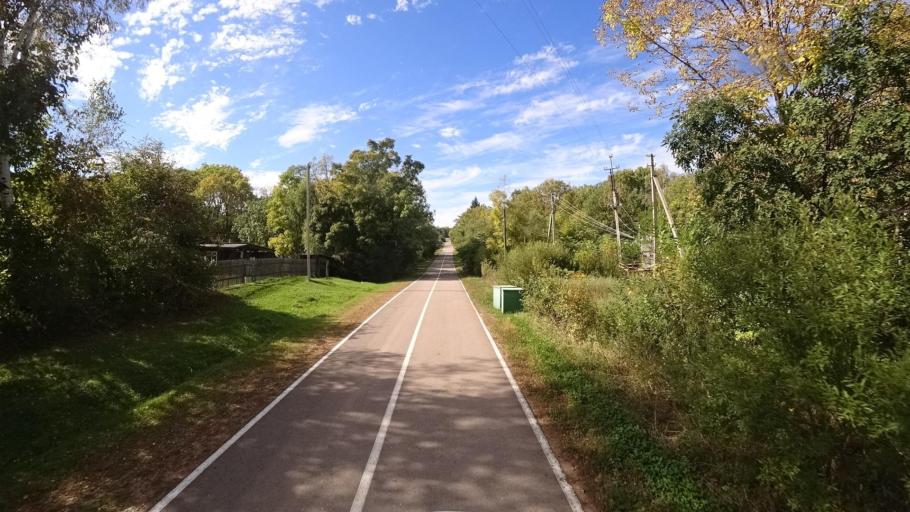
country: RU
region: Primorskiy
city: Yakovlevka
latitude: 44.3951
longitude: 133.6048
